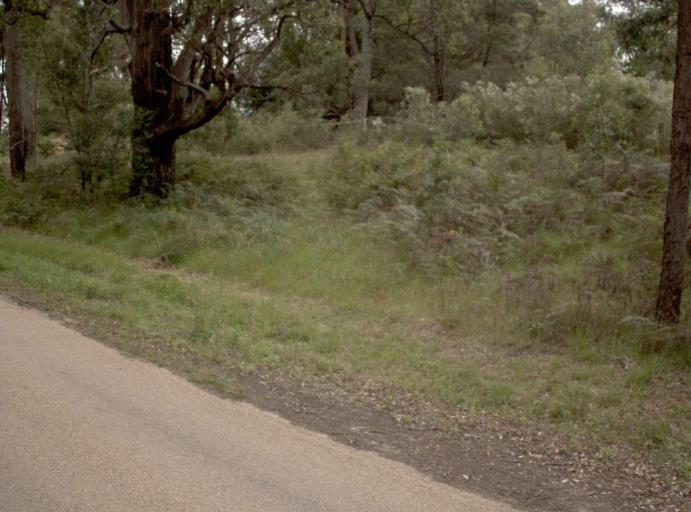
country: AU
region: Victoria
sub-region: East Gippsland
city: Bairnsdale
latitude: -37.7451
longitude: 147.5978
